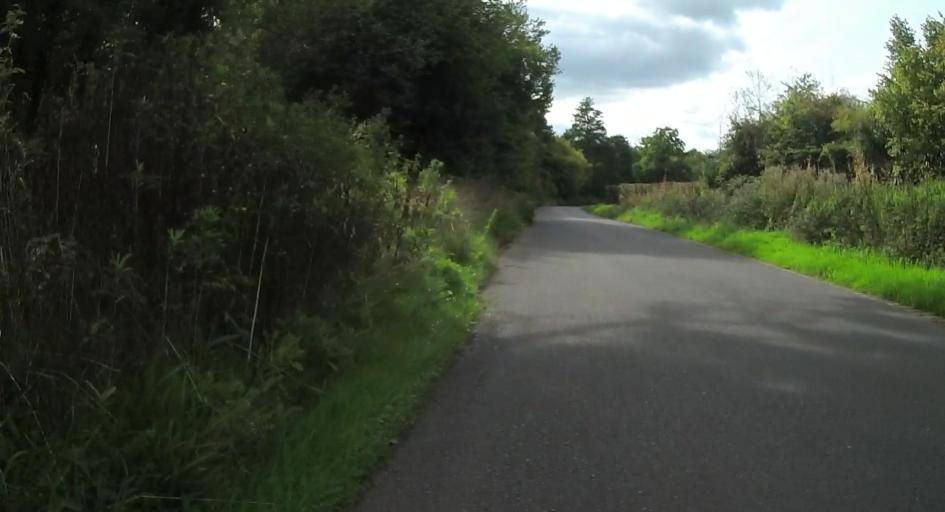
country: GB
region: England
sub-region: Surrey
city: Knaphill
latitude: 51.3378
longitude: -0.6259
